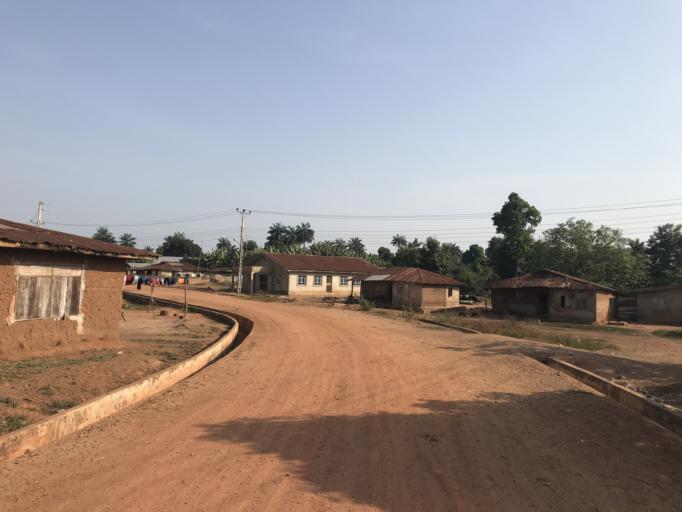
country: NG
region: Osun
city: Bode Osi
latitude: 7.7684
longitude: 4.3053
